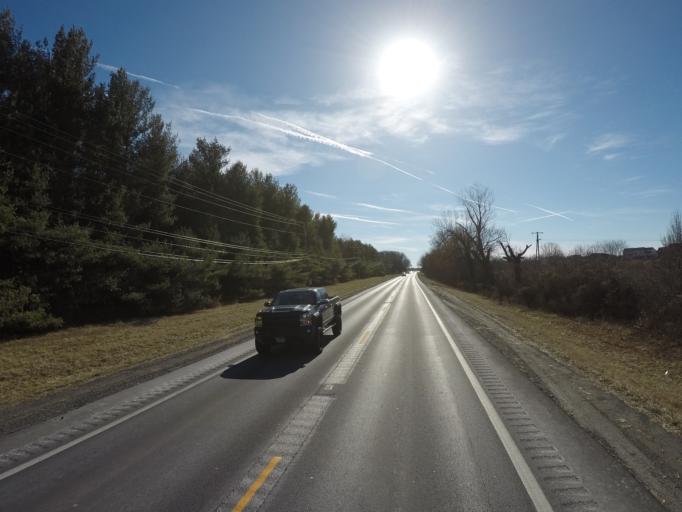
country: US
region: Virginia
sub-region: Loudoun County
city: Leesburg
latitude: 39.1595
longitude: -77.5376
